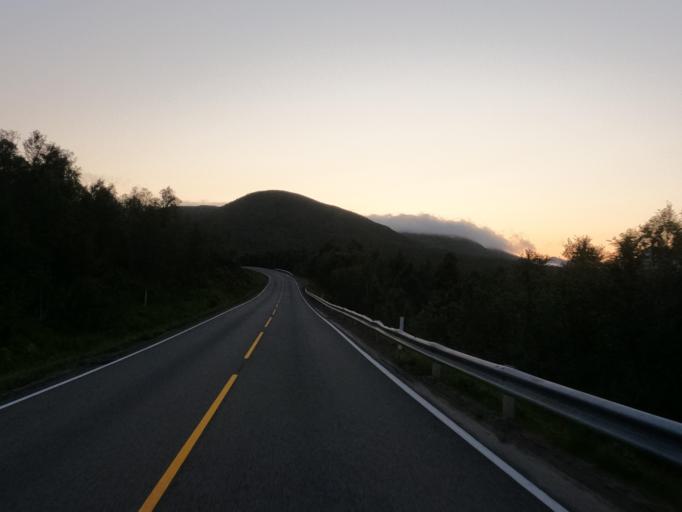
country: NO
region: Nordland
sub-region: Lodingen
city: Lodingen
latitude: 68.5198
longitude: 15.8618
